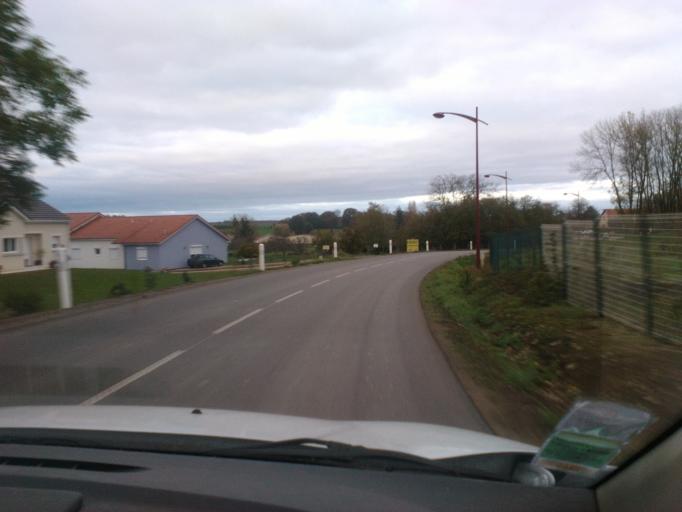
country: FR
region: Lorraine
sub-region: Departement des Vosges
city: Darnieulles
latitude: 48.2402
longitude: 6.3341
